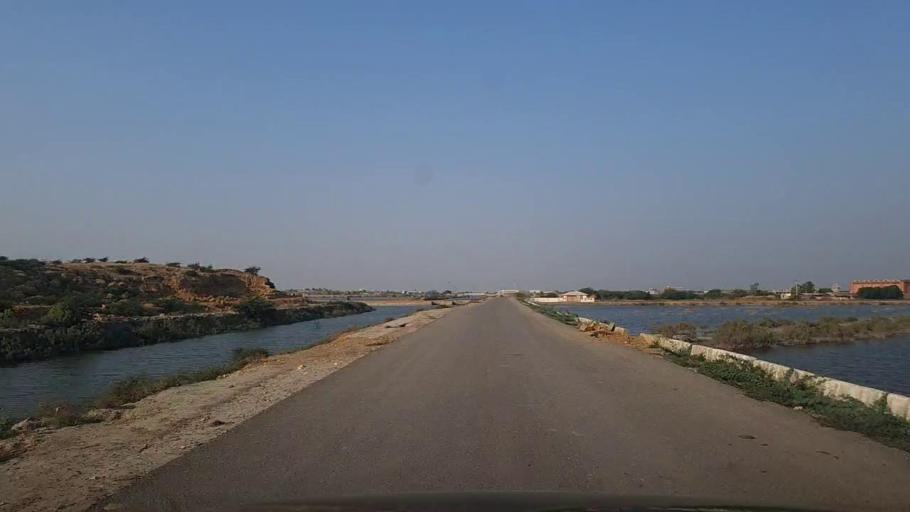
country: PK
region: Sindh
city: Thatta
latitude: 24.7431
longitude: 67.9068
